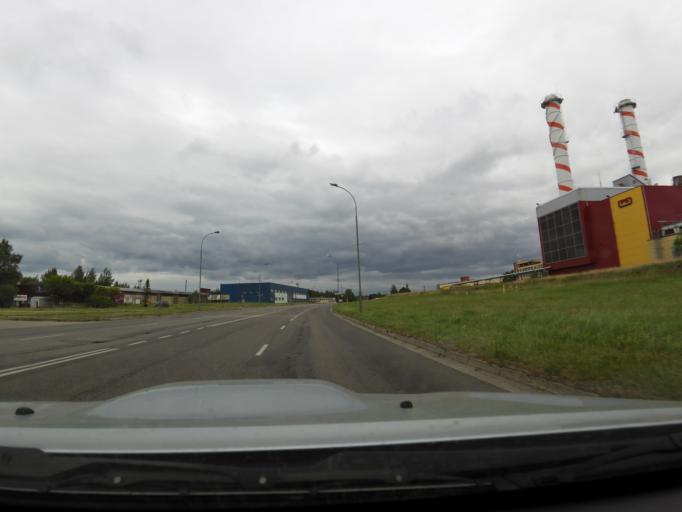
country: LT
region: Panevezys
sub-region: Panevezys City
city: Panevezys
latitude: 55.7478
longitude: 24.3822
